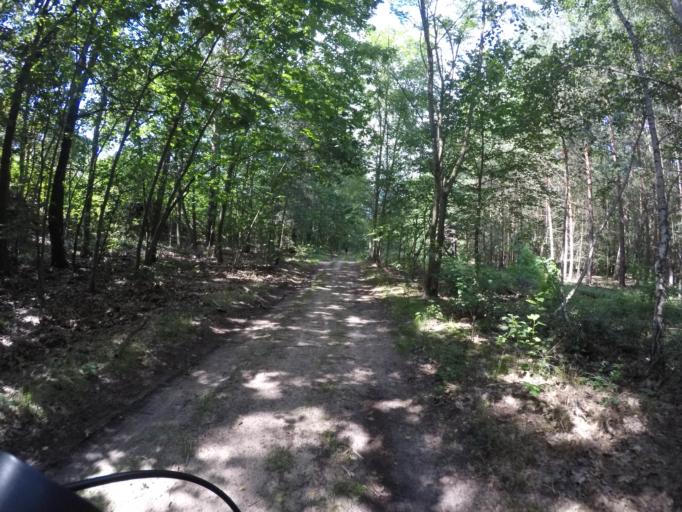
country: DE
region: Brandenburg
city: Potsdam
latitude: 52.3760
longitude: 13.0052
